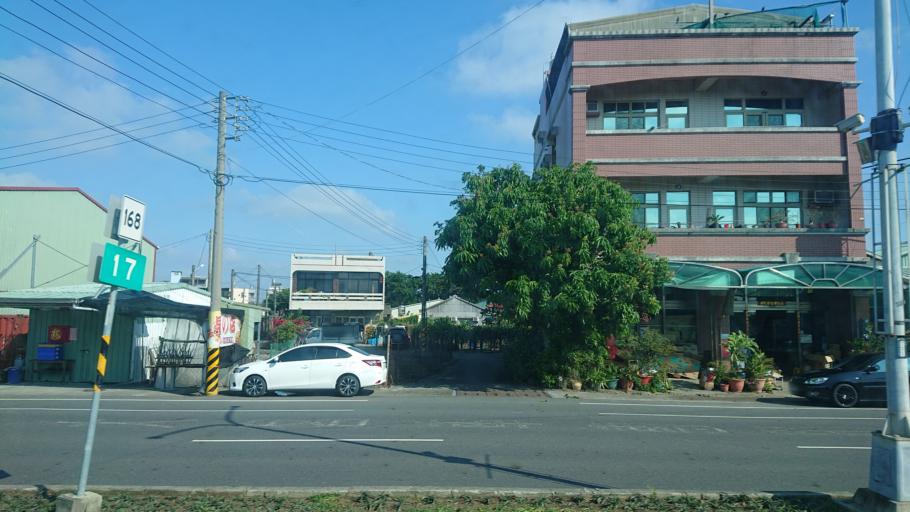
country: TW
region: Taiwan
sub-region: Chiayi
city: Taibao
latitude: 23.4574
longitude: 120.3106
